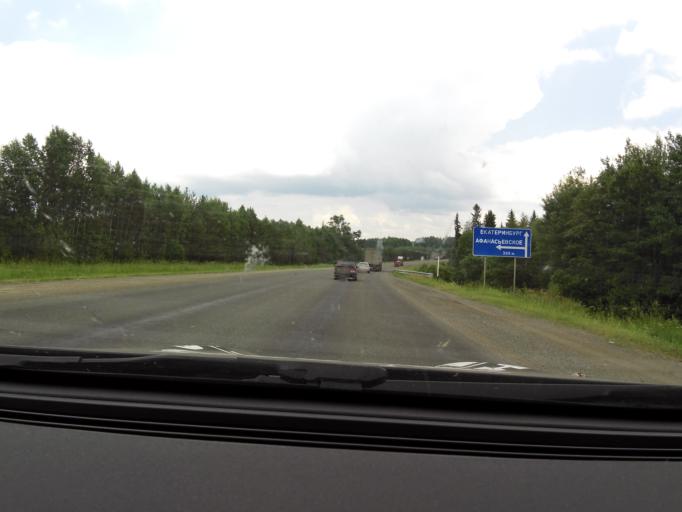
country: RU
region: Sverdlovsk
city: Ufimskiy
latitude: 56.7807
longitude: 58.2615
